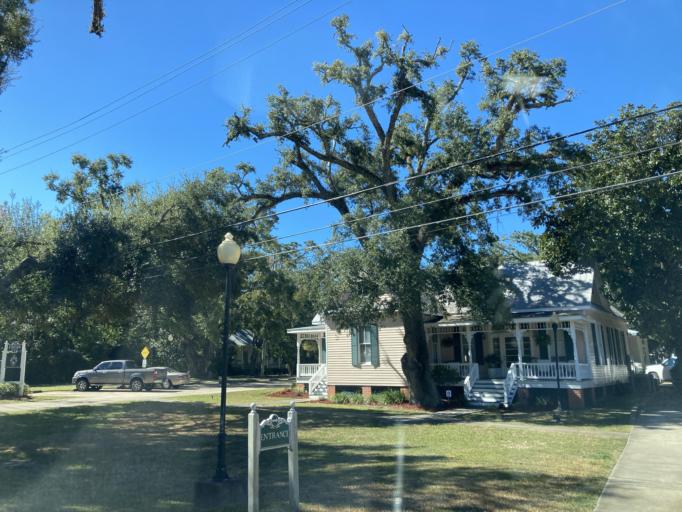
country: US
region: Mississippi
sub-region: Jackson County
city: Ocean Springs
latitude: 30.4122
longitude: -88.8296
